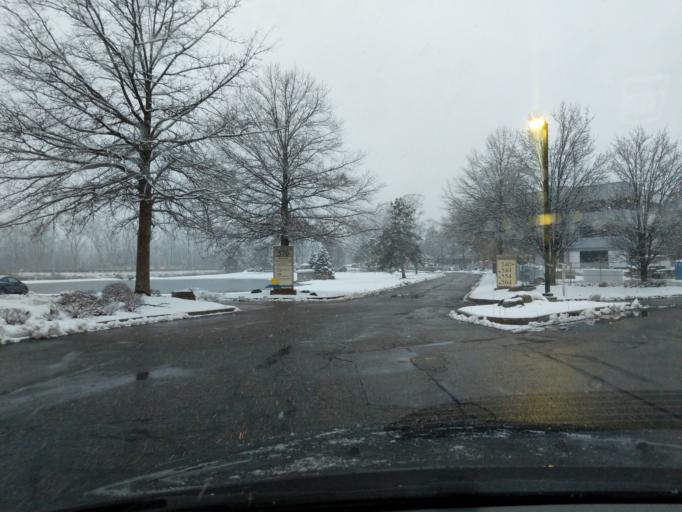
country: US
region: Ohio
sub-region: Summit County
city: Fairlawn
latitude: 41.1019
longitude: -81.5870
